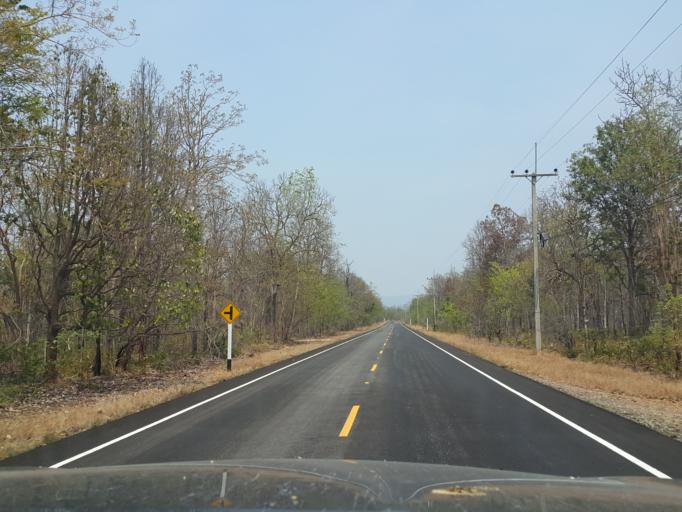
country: TH
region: Lampang
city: Mae Phrik
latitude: 17.5511
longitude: 99.1221
